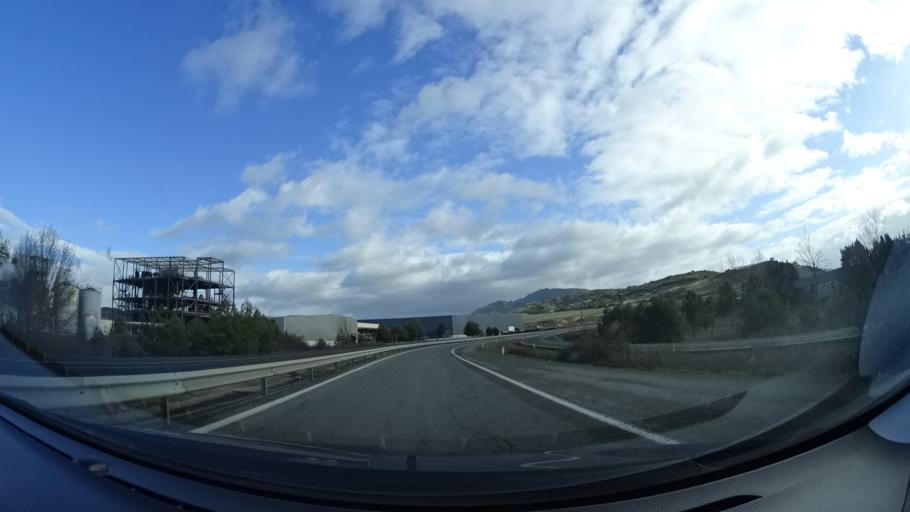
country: ES
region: Basque Country
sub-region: Provincia de Alava
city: Zambrana
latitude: 42.6748
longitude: -2.8895
